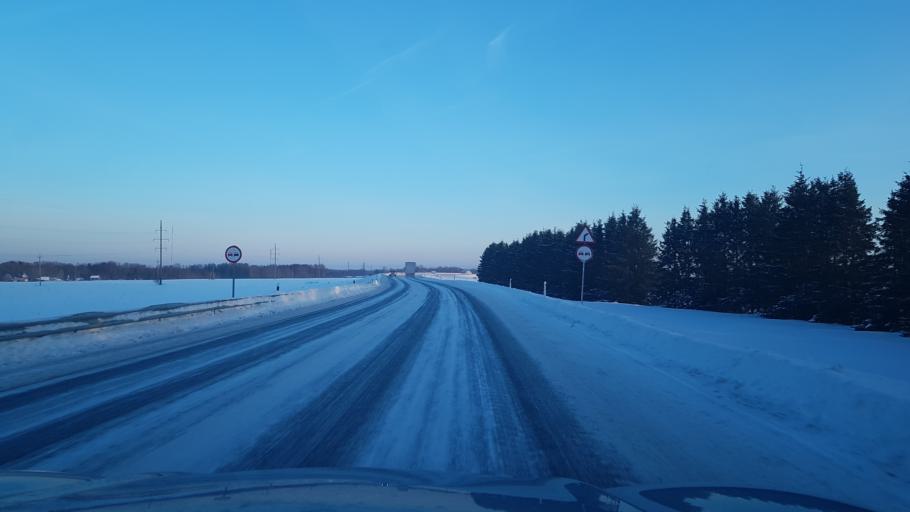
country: EE
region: Ida-Virumaa
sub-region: Narva-Joesuu linn
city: Narva-Joesuu
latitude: 59.4051
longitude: 28.0460
